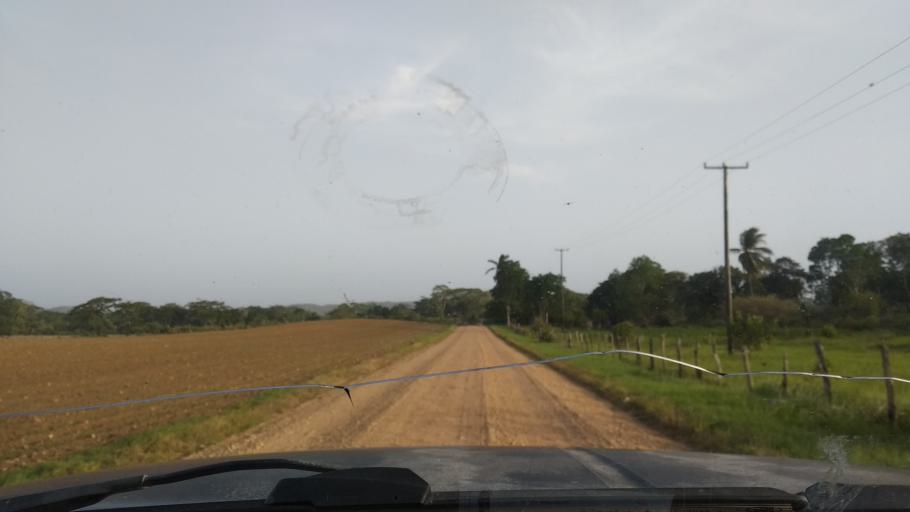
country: BZ
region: Cayo
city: San Ignacio
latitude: 17.2096
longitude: -89.0138
